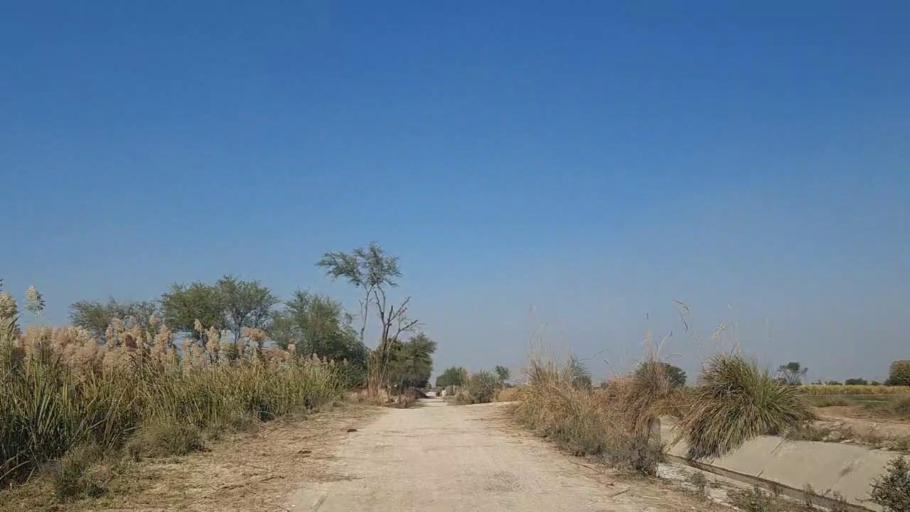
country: PK
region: Sindh
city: Sakrand
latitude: 26.2660
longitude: 68.2210
